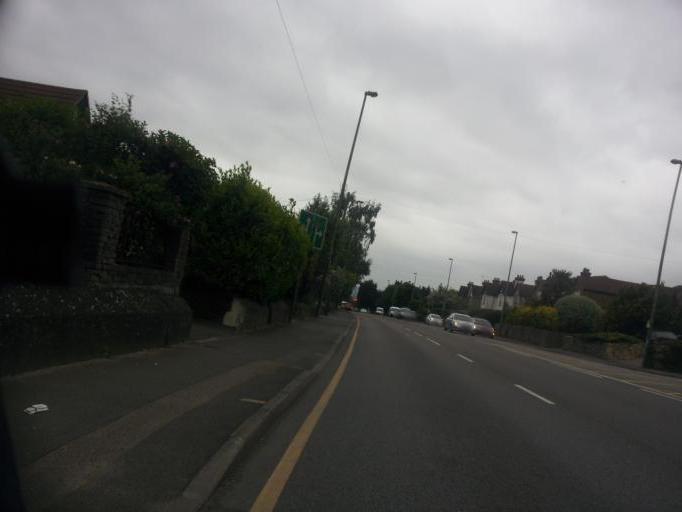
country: GB
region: England
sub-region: Kent
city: Maidstone
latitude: 51.2600
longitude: 0.5303
